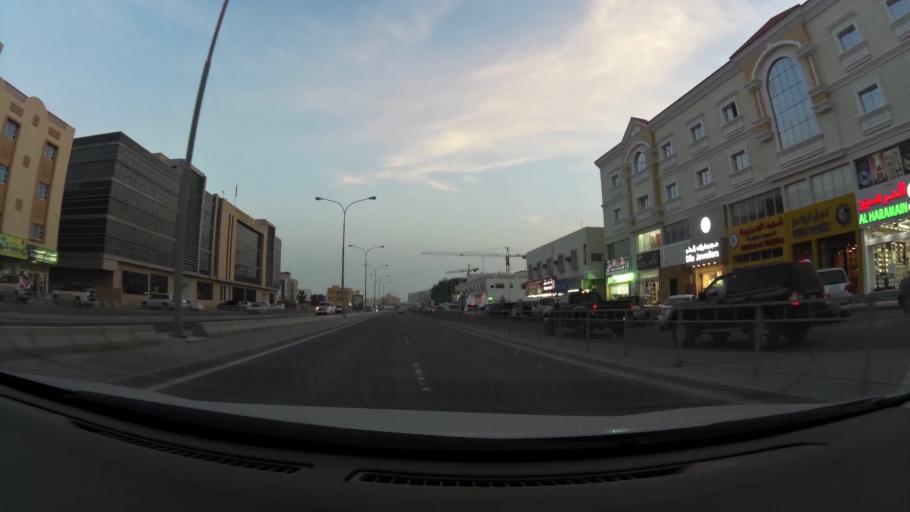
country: QA
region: Al Wakrah
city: Al Wakrah
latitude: 25.1679
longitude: 51.5977
